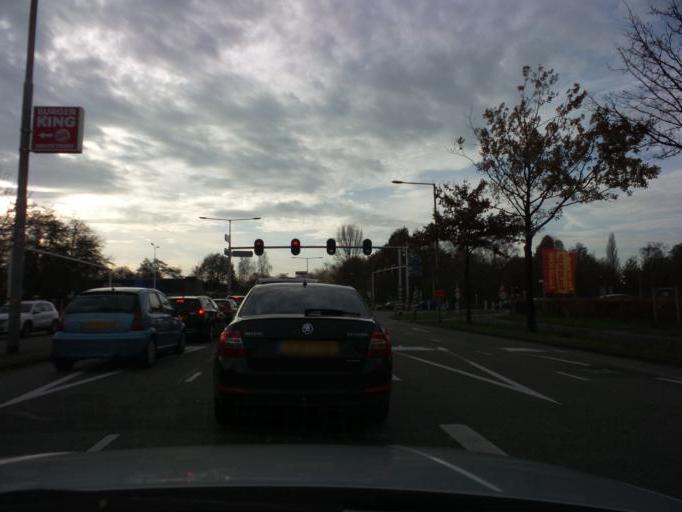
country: NL
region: Utrecht
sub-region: Gemeente Amersfoort
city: Hoogland
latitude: 52.1652
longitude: 5.3579
